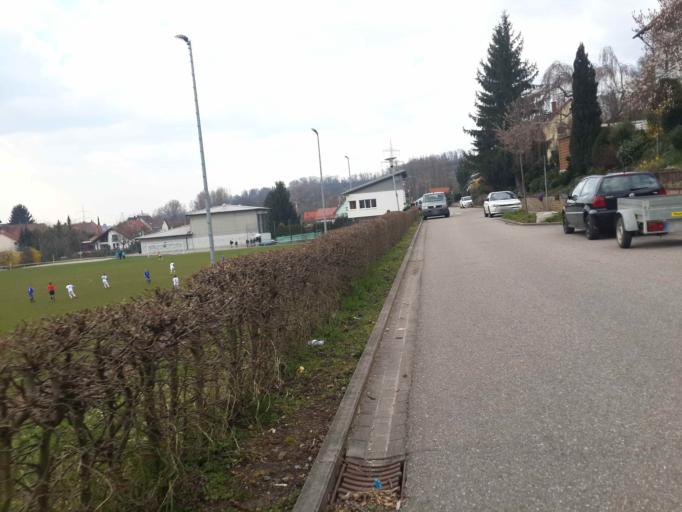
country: DE
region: Baden-Wuerttemberg
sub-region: Karlsruhe Region
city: Balzfeld
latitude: 49.2114
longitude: 8.8068
